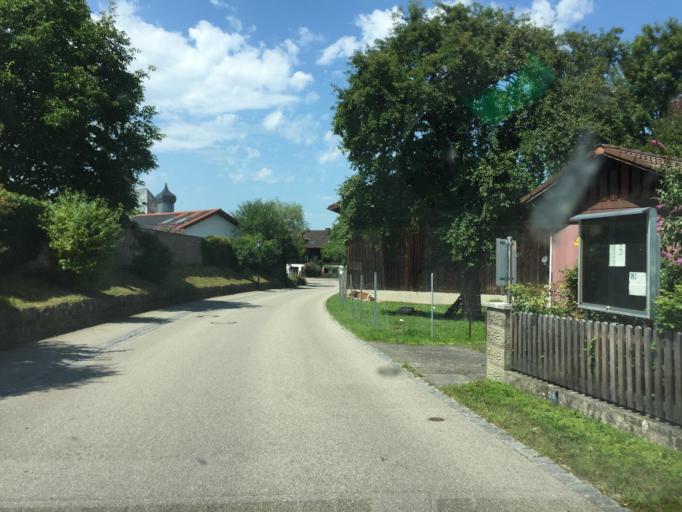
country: DE
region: Bavaria
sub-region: Upper Bavaria
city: Tuntenhausen
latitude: 47.9346
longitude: 12.0177
